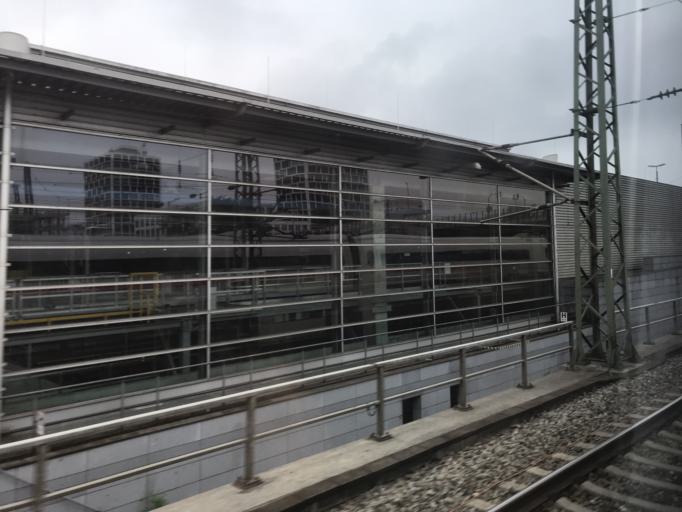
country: DE
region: Bavaria
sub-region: Upper Bavaria
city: Munich
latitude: 48.1429
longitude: 11.5214
